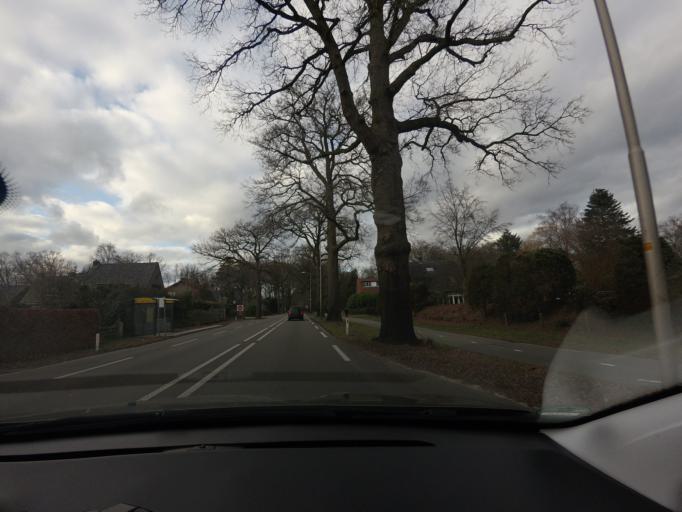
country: NL
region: Gelderland
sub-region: Gemeente Lochem
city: Gorssel
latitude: 52.1864
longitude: 6.2102
